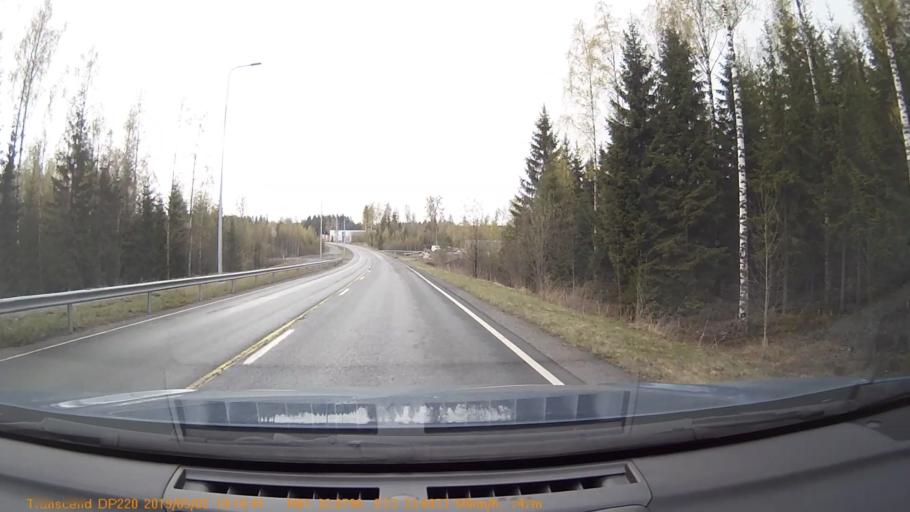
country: FI
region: Pirkanmaa
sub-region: Tampere
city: Yloejaervi
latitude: 61.5347
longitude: 23.5650
